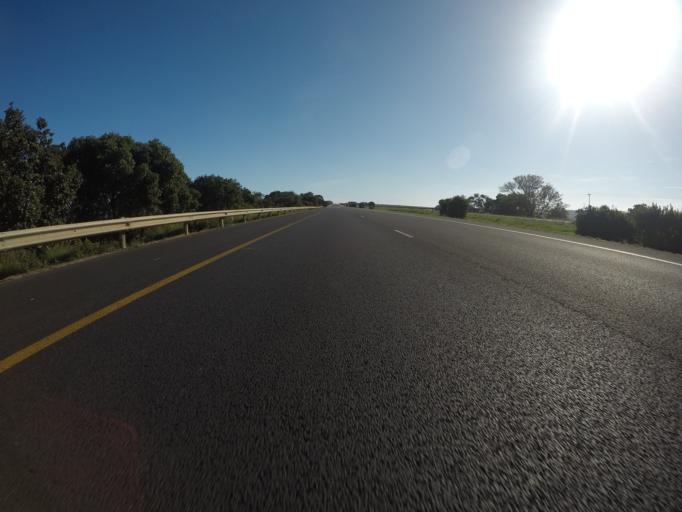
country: ZA
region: Western Cape
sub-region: Eden District Municipality
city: Mossel Bay
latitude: -34.1652
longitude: 22.0871
